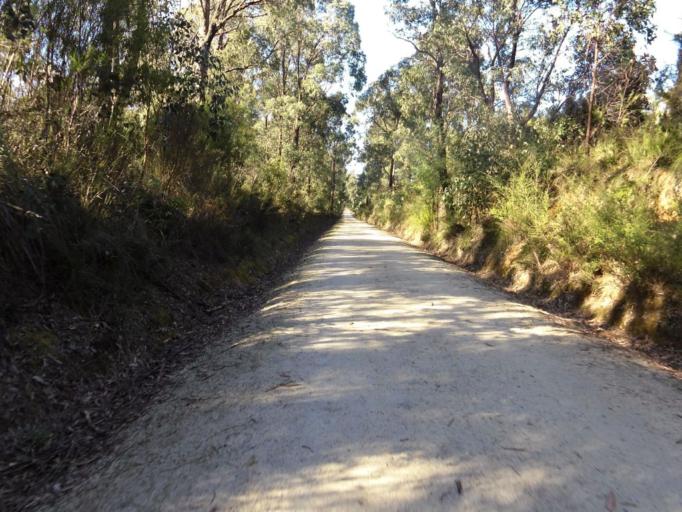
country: AU
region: Victoria
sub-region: Latrobe
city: Moe
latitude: -38.3750
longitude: 146.1983
